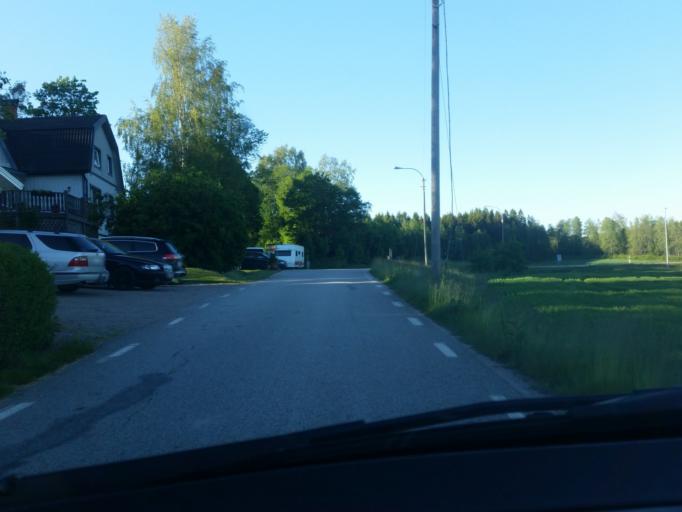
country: SE
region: Vaestra Goetaland
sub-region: Fargelanda Kommun
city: Faergelanda
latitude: 58.5162
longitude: 11.9819
